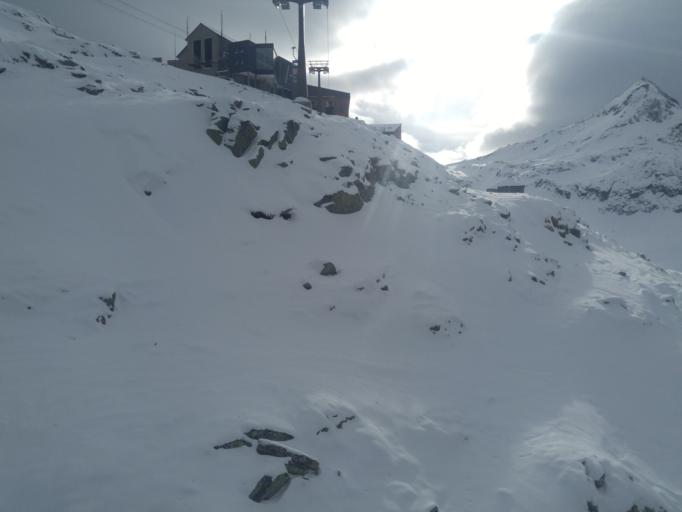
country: AT
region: Salzburg
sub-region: Politischer Bezirk Zell am See
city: Niedernsill
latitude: 47.1371
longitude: 12.6255
